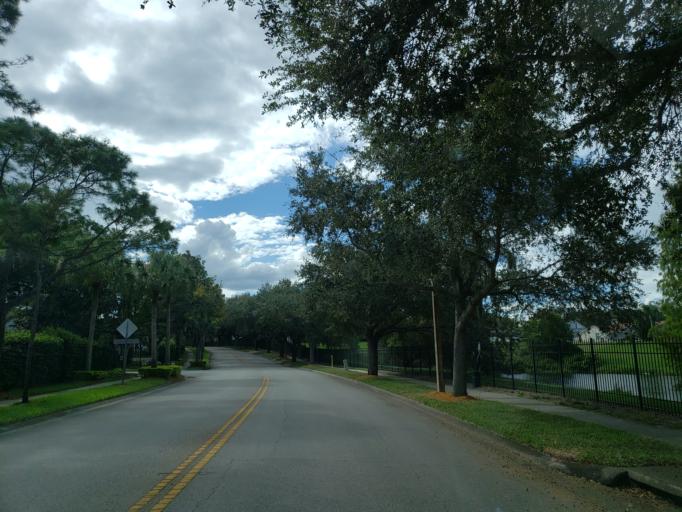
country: US
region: Florida
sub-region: Hillsborough County
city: Bloomingdale
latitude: 27.8743
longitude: -82.2482
